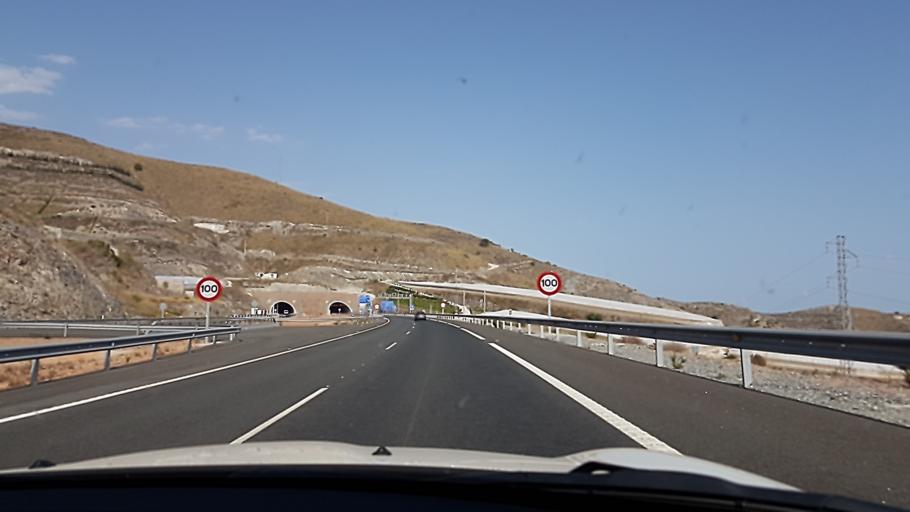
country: ES
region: Andalusia
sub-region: Provincia de Granada
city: Gualchos
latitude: 36.7156
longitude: -3.4490
